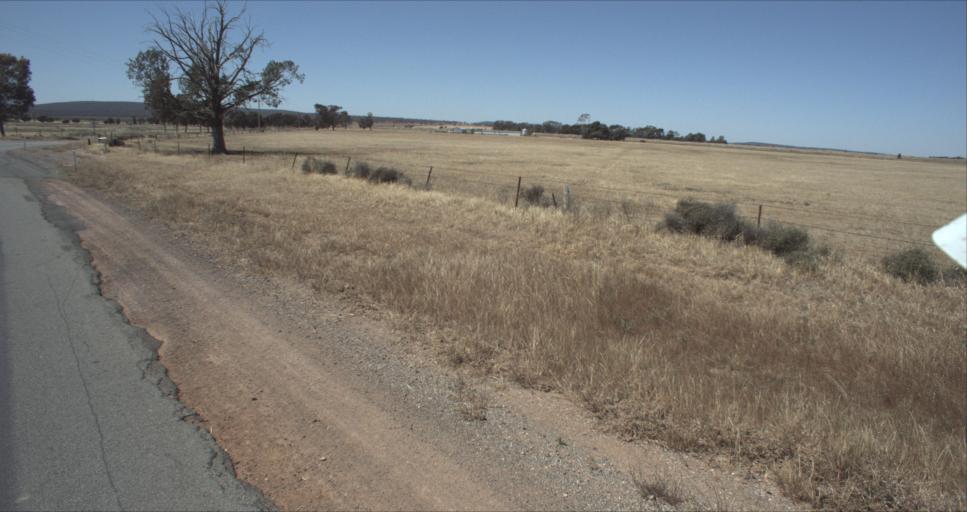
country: AU
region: New South Wales
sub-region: Leeton
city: Leeton
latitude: -34.5342
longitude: 146.4464
